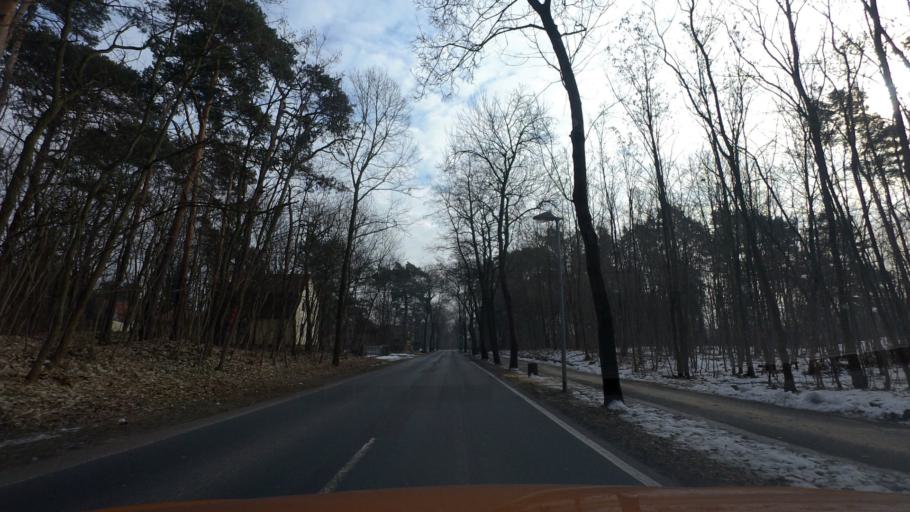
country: DE
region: Brandenburg
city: Zossen
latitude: 52.2439
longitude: 13.4250
